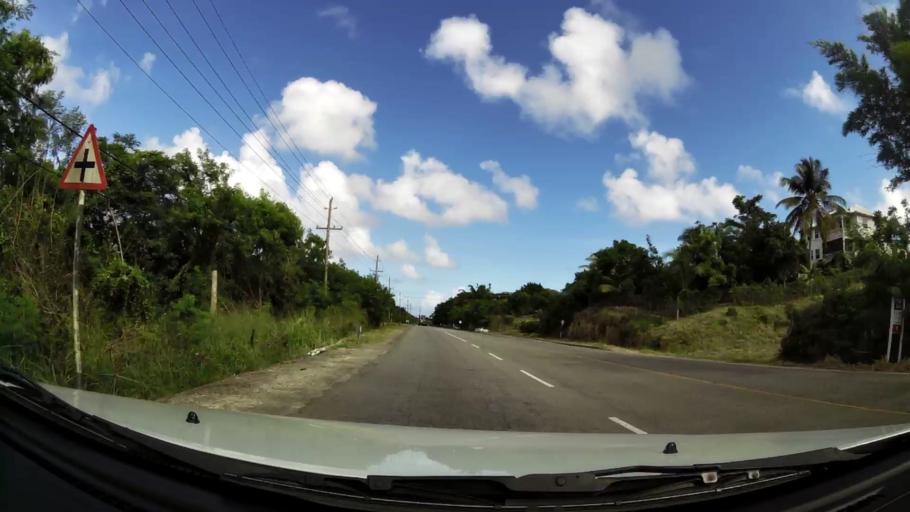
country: BB
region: Saint Peter
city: Speightstown
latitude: 13.2506
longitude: -59.6235
